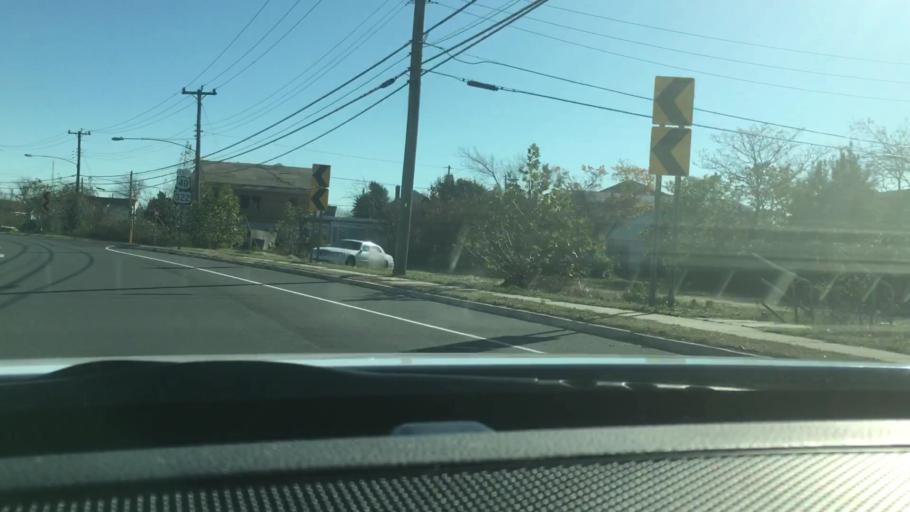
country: US
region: New Jersey
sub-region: Atlantic County
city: Pleasantville
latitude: 39.3861
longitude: -74.5134
